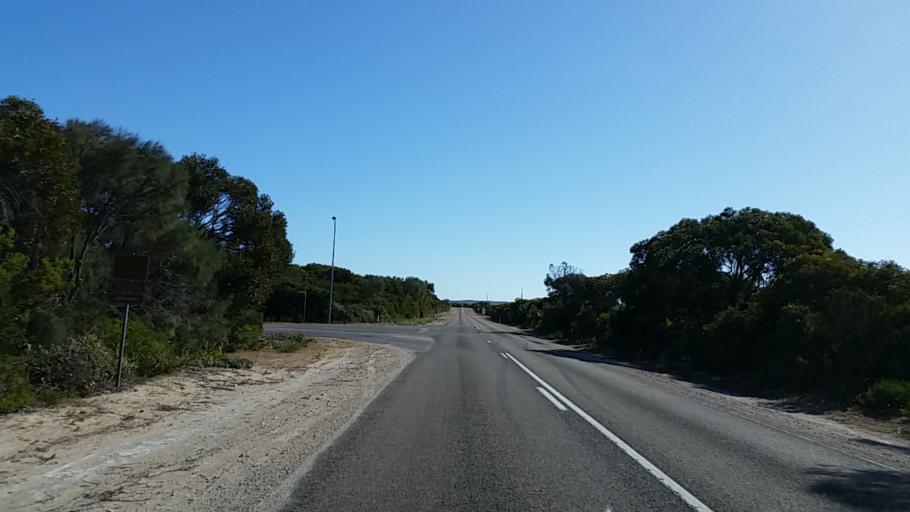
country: AU
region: South Australia
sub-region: Yorke Peninsula
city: Honiton
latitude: -35.2488
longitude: 136.9687
